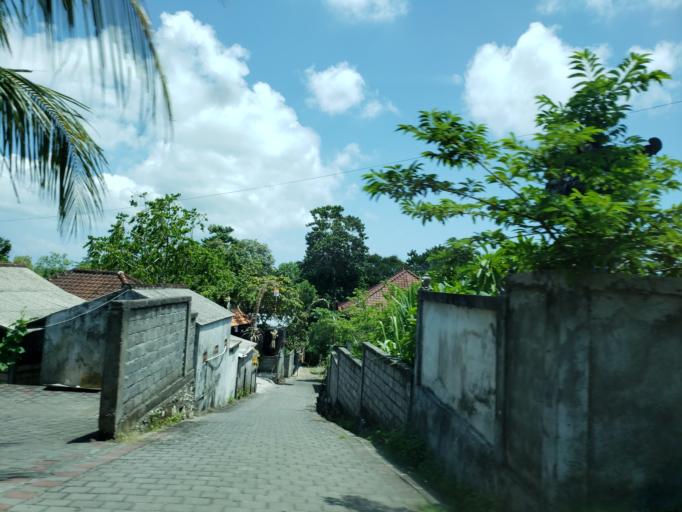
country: ID
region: Bali
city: Kangin
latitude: -8.8354
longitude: 115.1364
